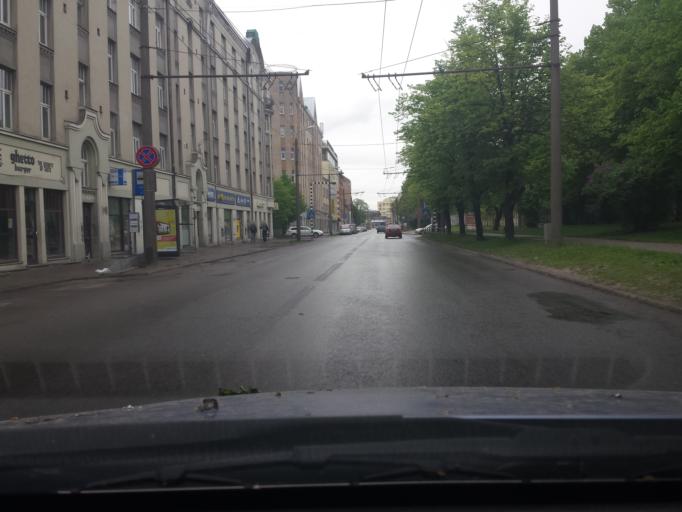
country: LV
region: Riga
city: Riga
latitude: 56.9590
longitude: 24.1522
